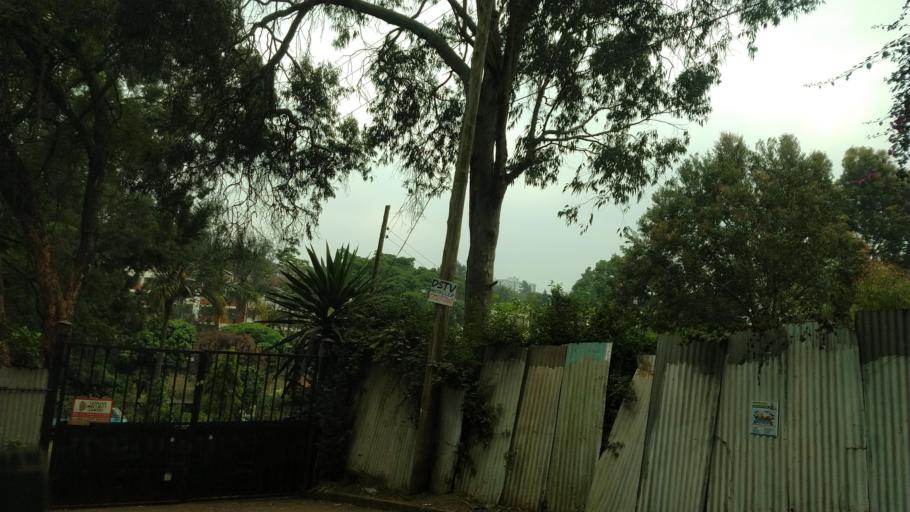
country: KE
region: Nairobi Area
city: Nairobi
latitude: -1.2941
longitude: 36.7766
